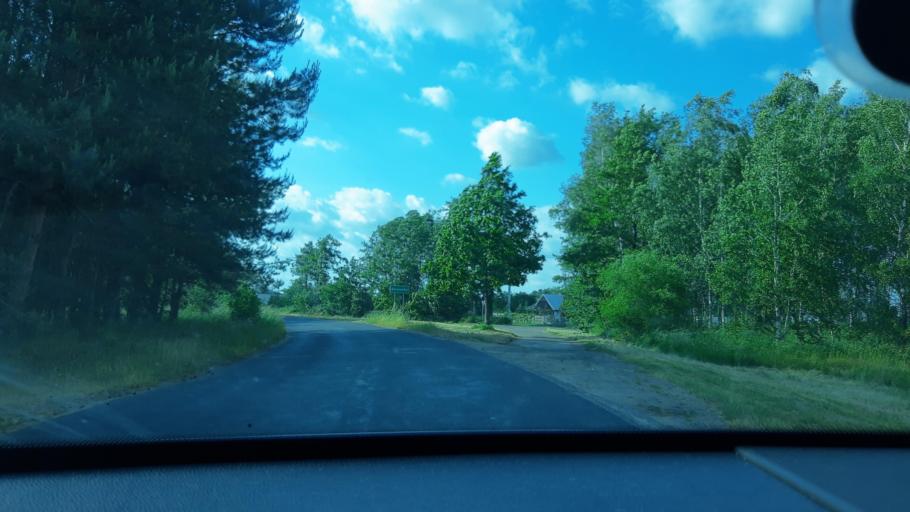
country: PL
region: Lodz Voivodeship
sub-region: Powiat zdunskowolski
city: Zapolice
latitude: 51.5334
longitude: 18.8368
